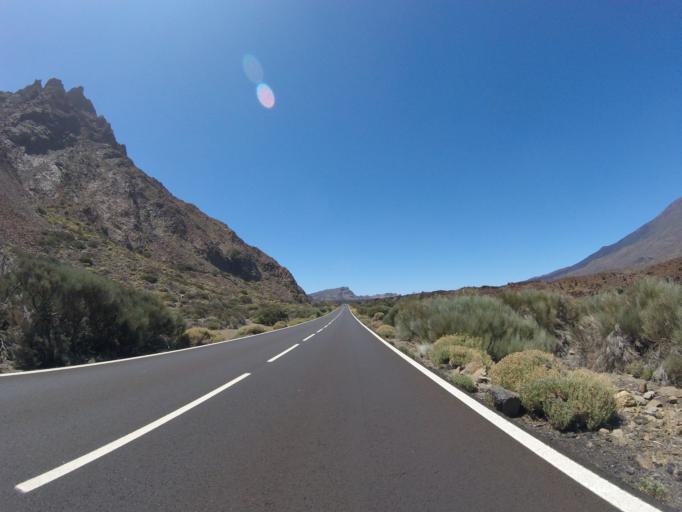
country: ES
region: Canary Islands
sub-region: Provincia de Santa Cruz de Tenerife
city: Vilaflor
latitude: 28.2142
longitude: -16.6645
